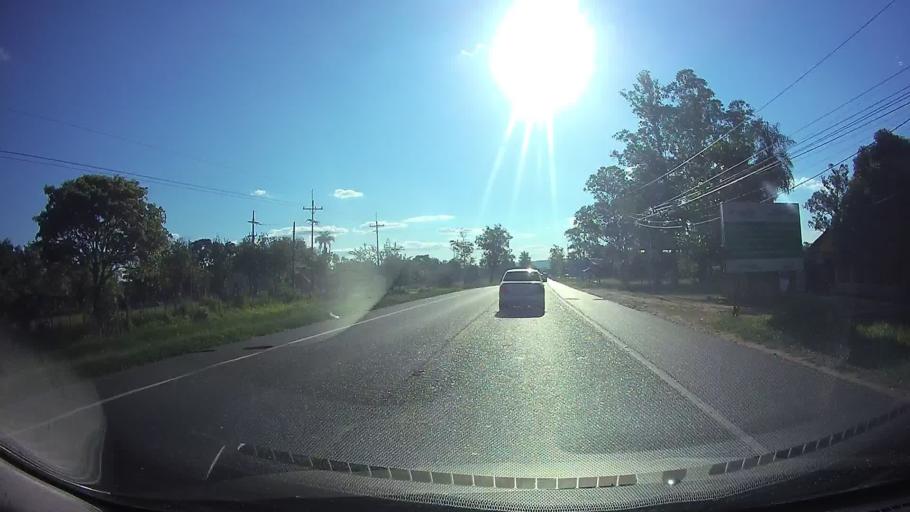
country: PY
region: Central
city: Ypacarai
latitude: -25.3781
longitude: -57.2390
